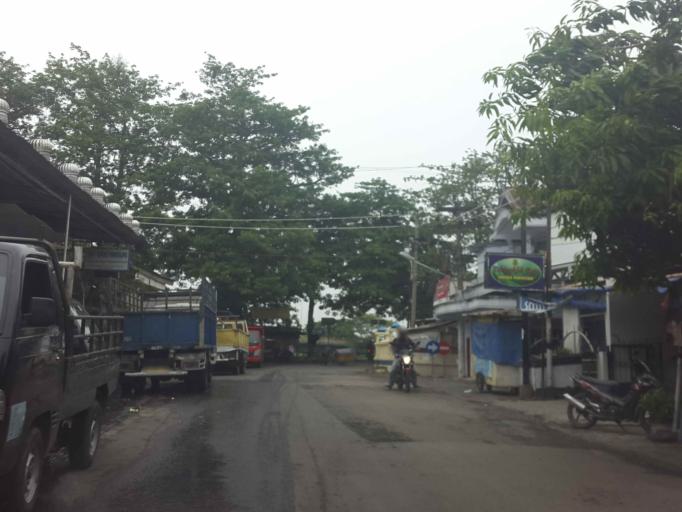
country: ID
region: Central Java
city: Semarang
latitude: -6.9727
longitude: 110.4441
